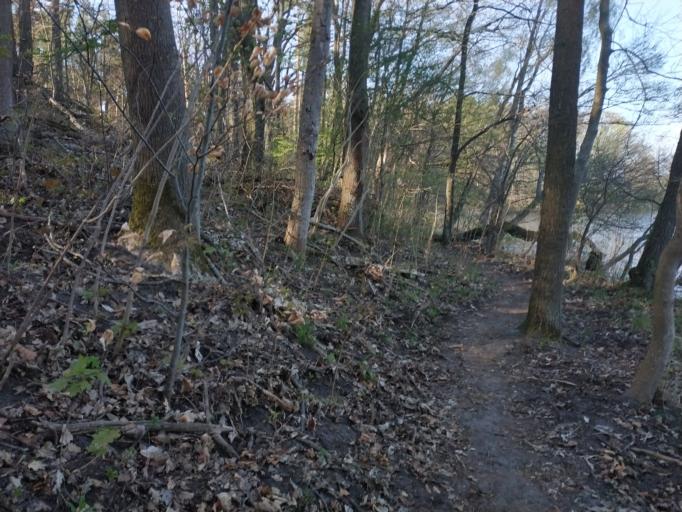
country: DE
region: Brandenburg
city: Strausberg
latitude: 52.5712
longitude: 13.8262
